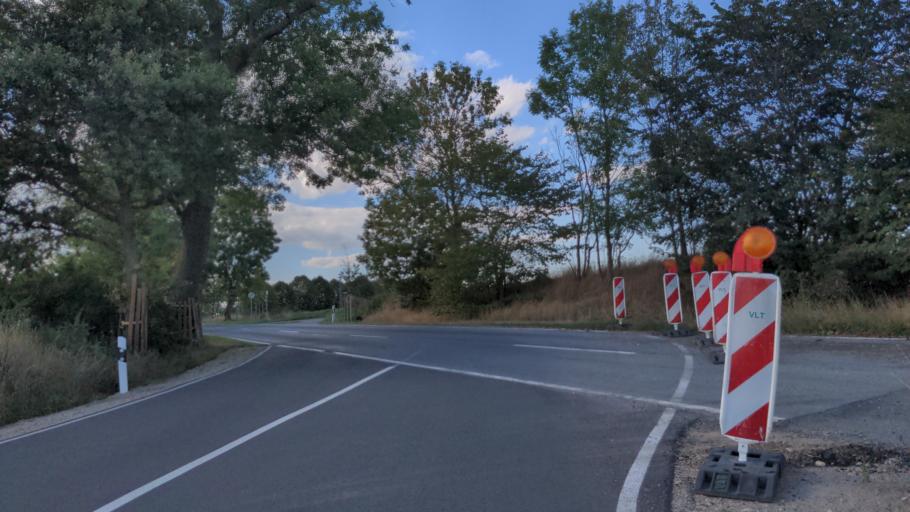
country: DE
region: Mecklenburg-Vorpommern
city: Klutz
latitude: 53.9612
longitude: 11.1894
